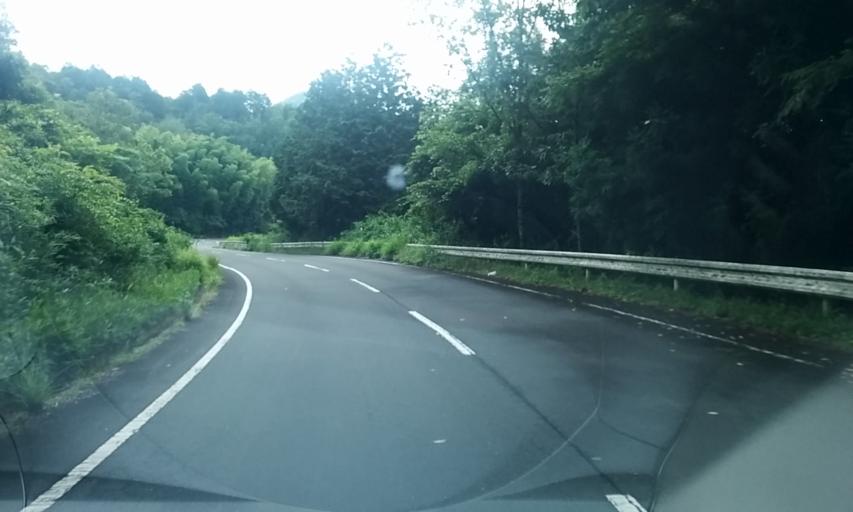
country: JP
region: Kyoto
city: Kameoka
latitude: 35.0896
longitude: 135.4342
